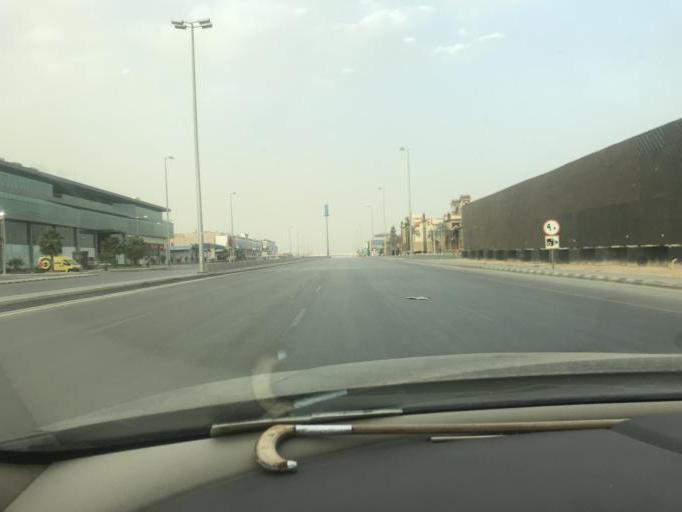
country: SA
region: Ar Riyad
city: Riyadh
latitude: 24.8066
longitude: 46.6614
